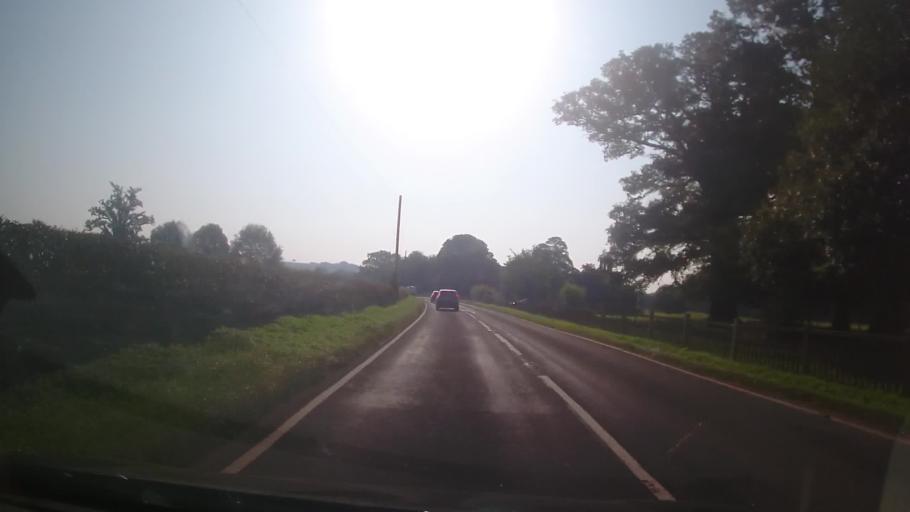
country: GB
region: England
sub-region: Shropshire
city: Alveley
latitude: 52.4965
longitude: -2.3685
